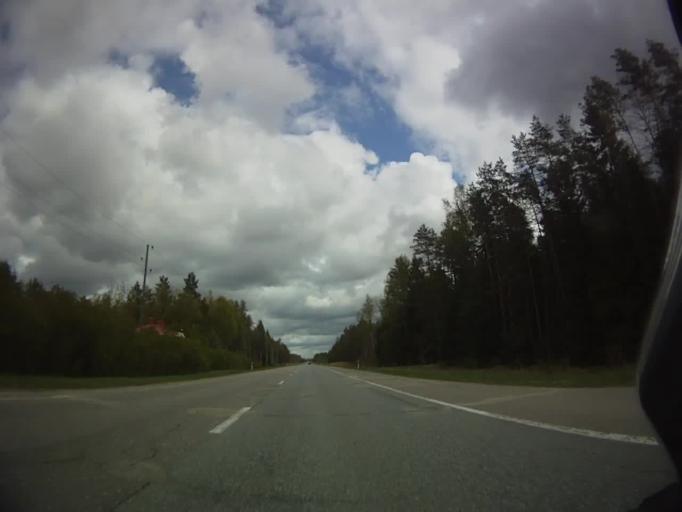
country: LV
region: Incukalns
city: Vangazi
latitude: 57.1064
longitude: 24.6057
